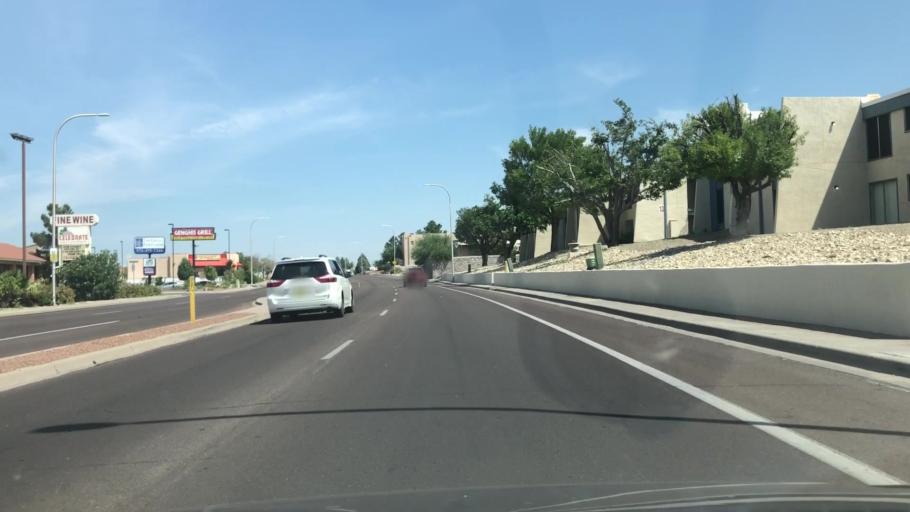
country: US
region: New Mexico
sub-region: Dona Ana County
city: University Park
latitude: 32.3066
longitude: -106.7386
